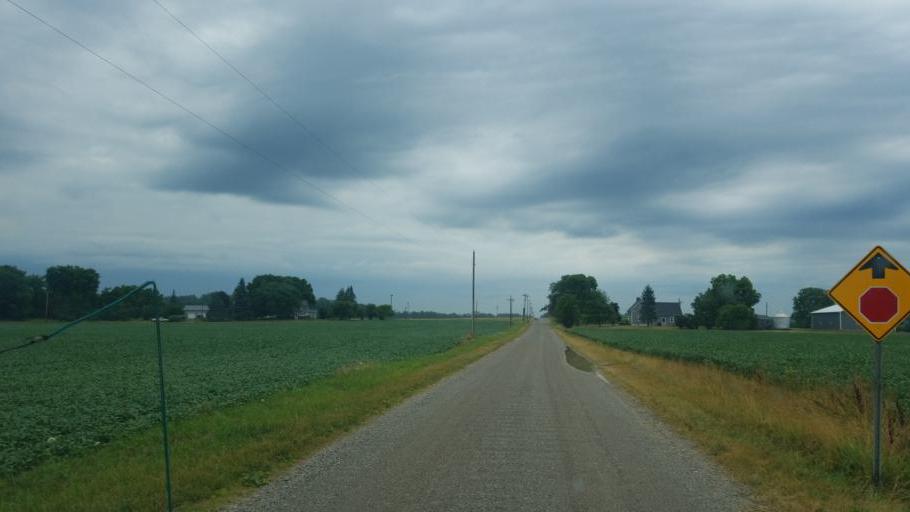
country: US
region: Indiana
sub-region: DeKalb County
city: Butler
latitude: 41.4430
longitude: -84.8984
